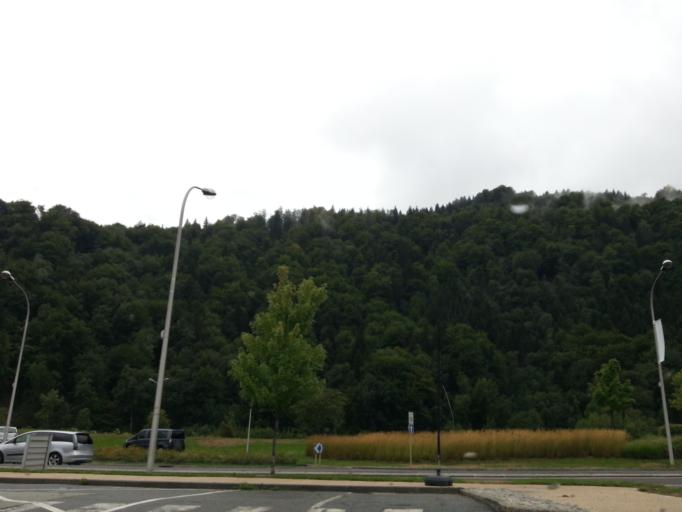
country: FR
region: Rhone-Alpes
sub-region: Departement de la Savoie
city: Ugine
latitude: 45.7471
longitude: 6.4172
